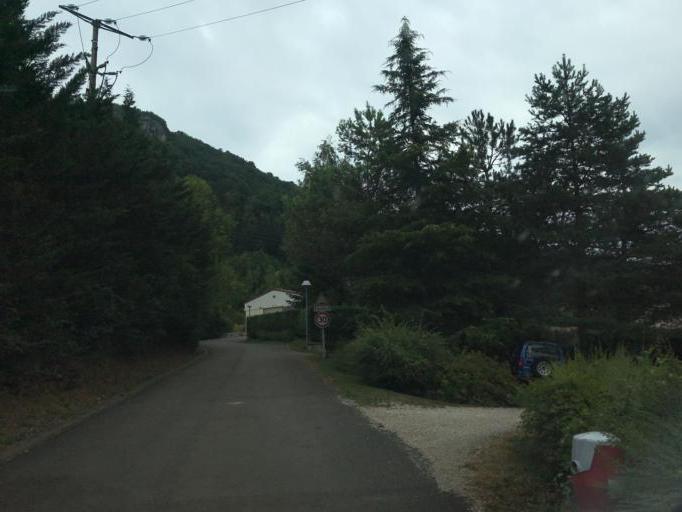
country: FR
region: Franche-Comte
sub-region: Departement du Jura
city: Lavans-les-Saint-Claude
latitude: 46.3610
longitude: 5.7859
